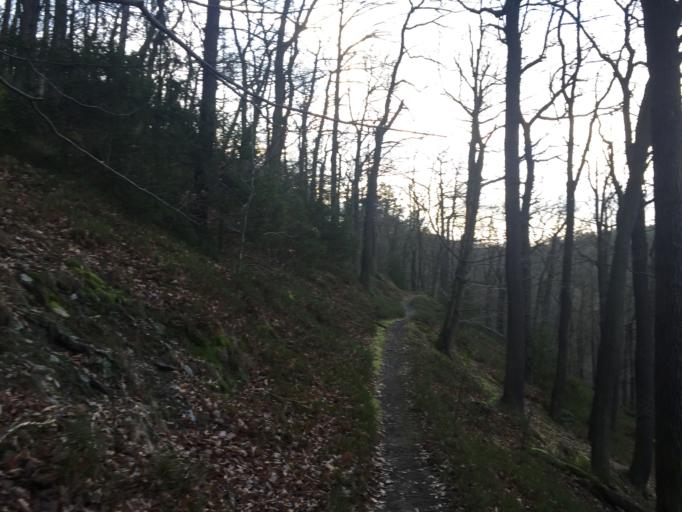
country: DE
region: Thuringia
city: Bad Blankenburg
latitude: 50.6648
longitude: 11.2534
